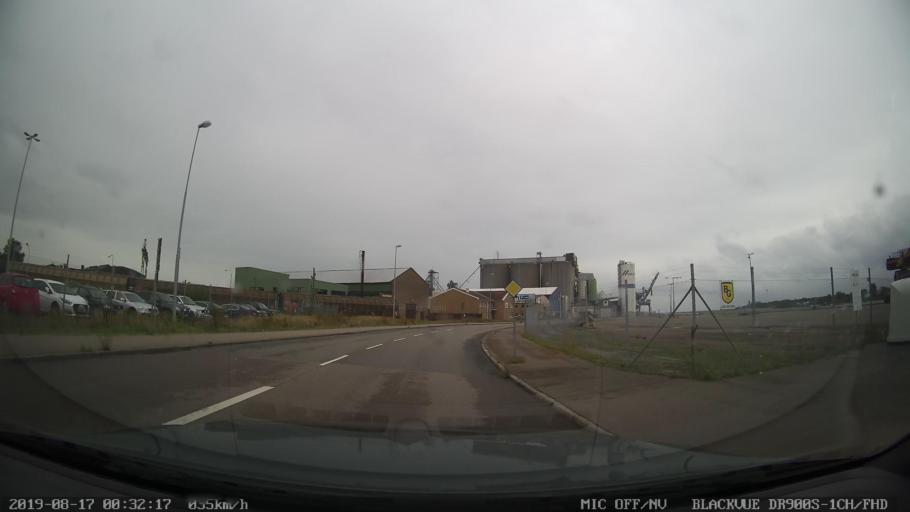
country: SE
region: Skane
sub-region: Landskrona
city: Landskrona
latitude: 55.8651
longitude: 12.8275
